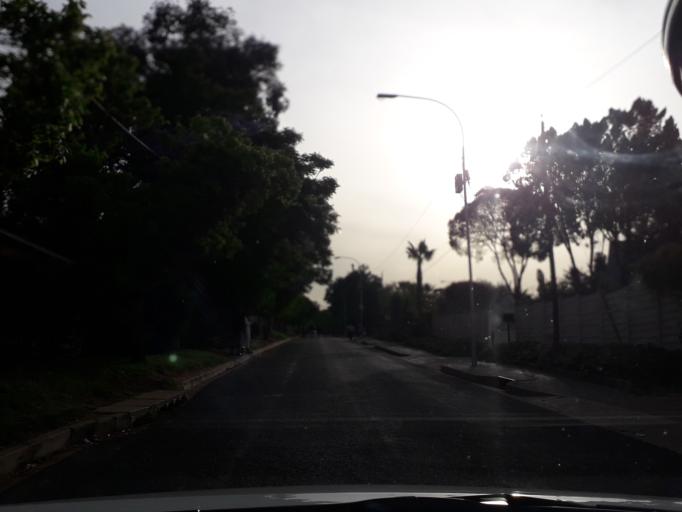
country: ZA
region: Gauteng
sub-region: City of Johannesburg Metropolitan Municipality
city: Modderfontein
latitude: -26.1278
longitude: 28.1173
